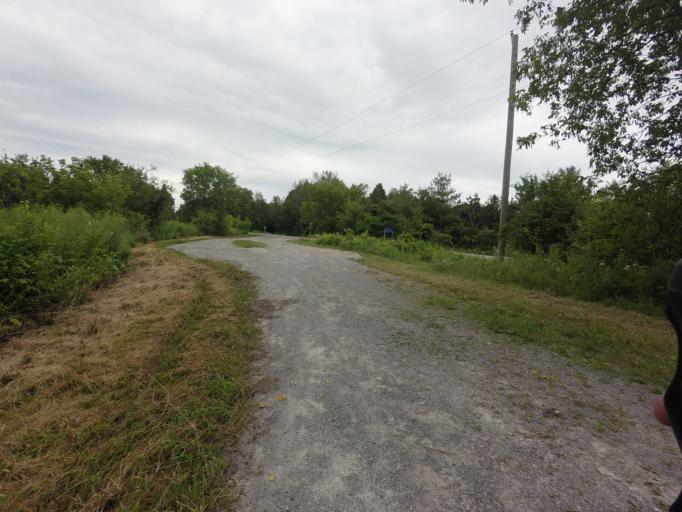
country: CA
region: Ontario
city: Ottawa
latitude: 45.2504
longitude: -75.6213
